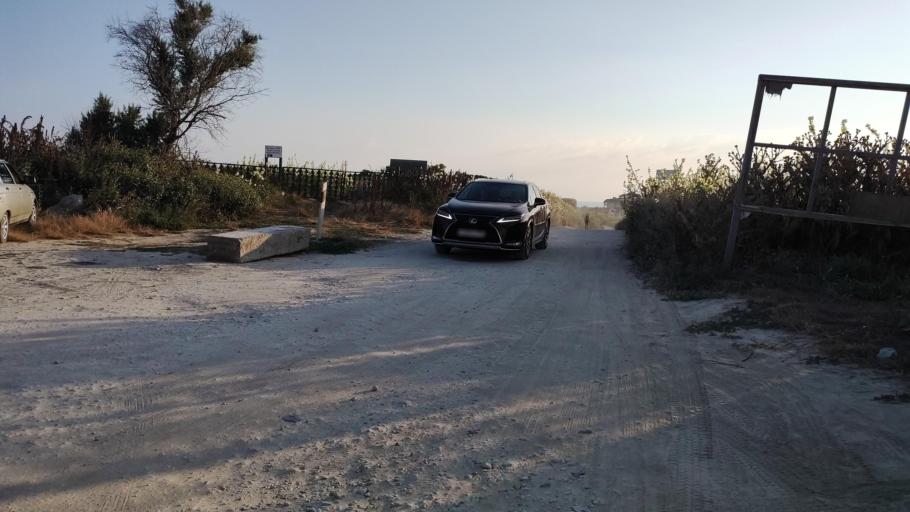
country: RU
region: Krasnodarskiy
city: Blagovetschenskaya
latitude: 45.0663
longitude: 37.0520
